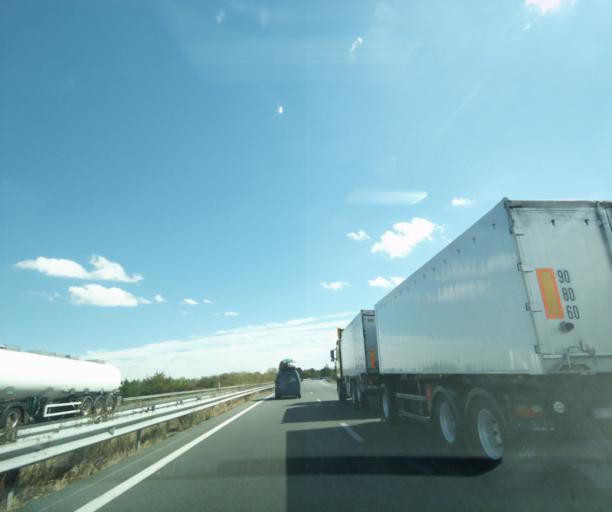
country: FR
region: Aquitaine
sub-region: Departement du Lot-et-Garonne
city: Tonneins
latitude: 44.3742
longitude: 0.2336
